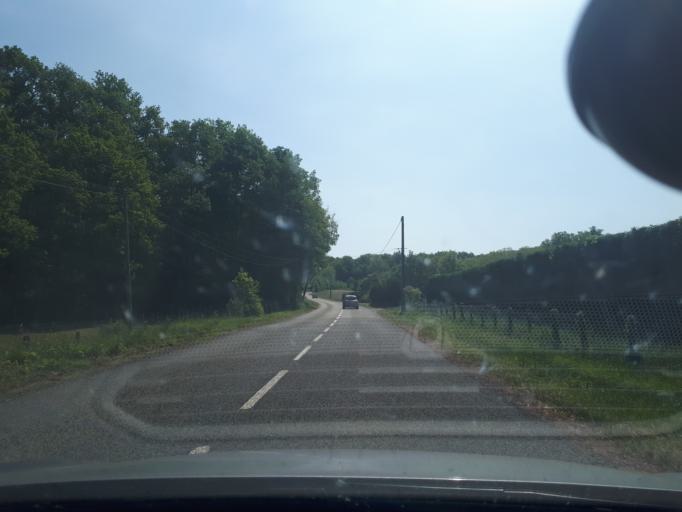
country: FR
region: Pays de la Loire
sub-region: Departement de la Sarthe
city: Montfort-le-Gesnois
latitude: 48.0346
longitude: 0.4366
